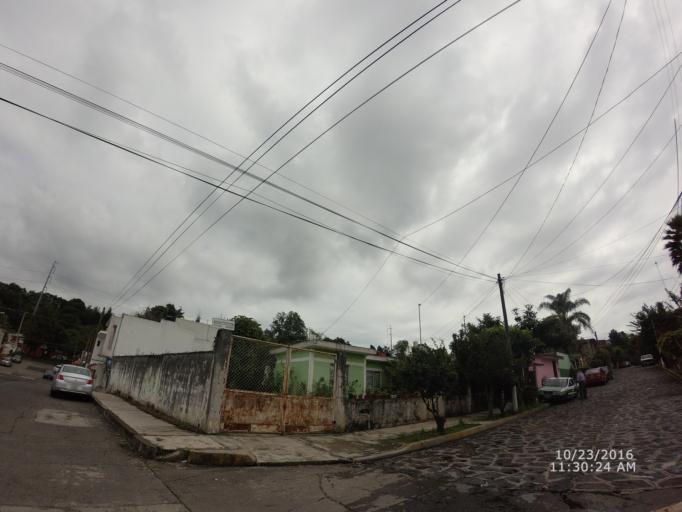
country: MX
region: Veracruz
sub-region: Tlalnelhuayocan
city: Guadalupe Victoria
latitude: 19.5487
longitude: -96.9379
